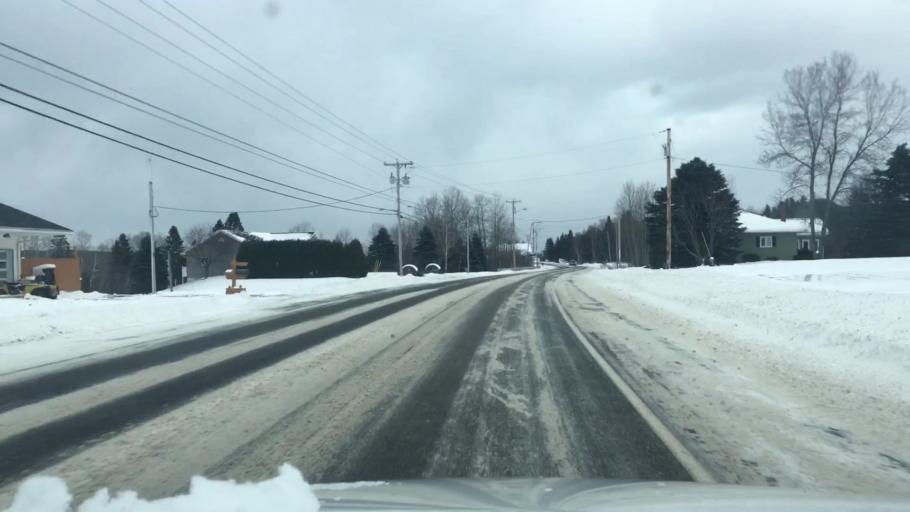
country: US
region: Maine
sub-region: Aroostook County
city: Madawaska
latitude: 47.3462
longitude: -68.2583
